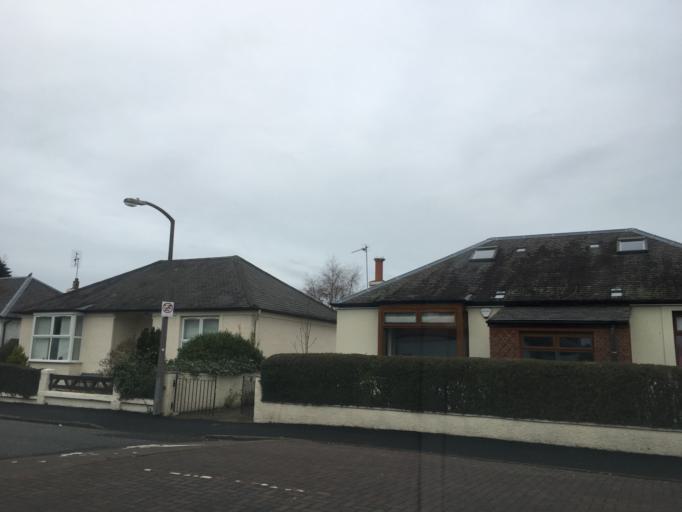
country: GB
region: Scotland
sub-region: Edinburgh
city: Colinton
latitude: 55.9405
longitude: -3.2472
